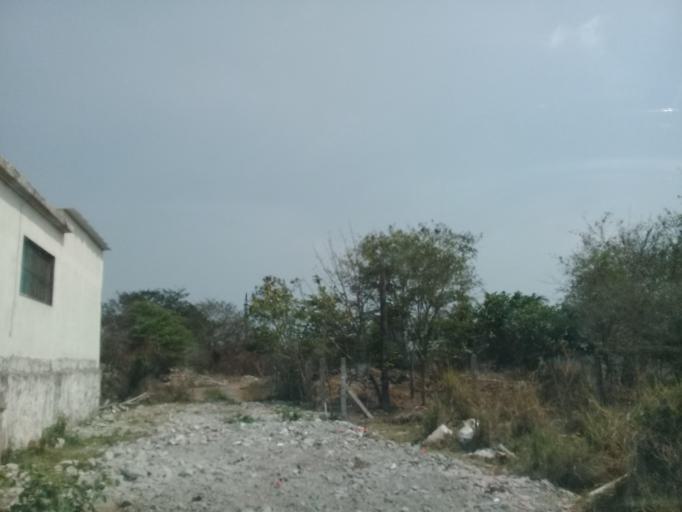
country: MX
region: Veracruz
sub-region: Veracruz
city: Hacienda Sotavento
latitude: 19.1322
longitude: -96.1770
